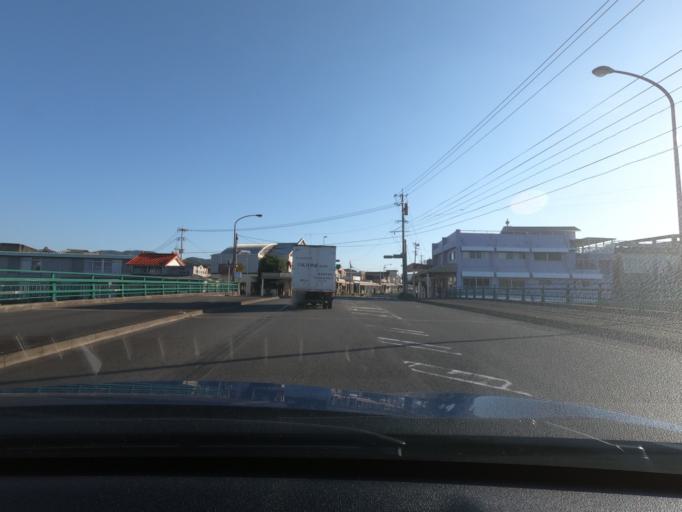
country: JP
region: Kagoshima
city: Akune
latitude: 32.0169
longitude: 130.1976
